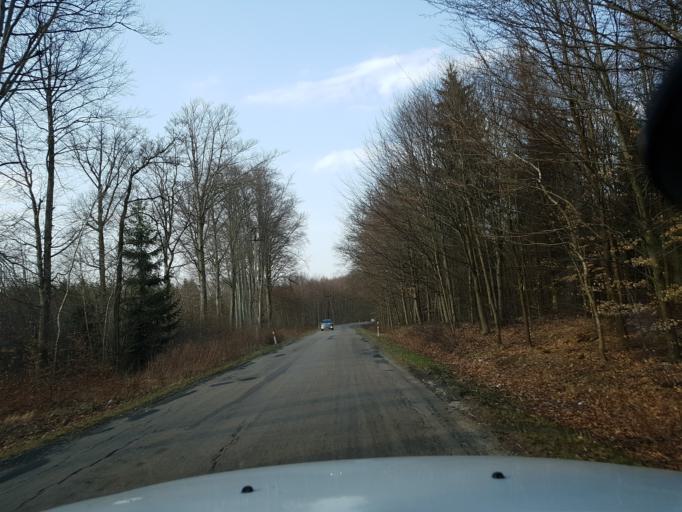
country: PL
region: West Pomeranian Voivodeship
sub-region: Powiat swidwinski
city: Polczyn-Zdroj
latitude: 53.7342
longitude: 16.0757
